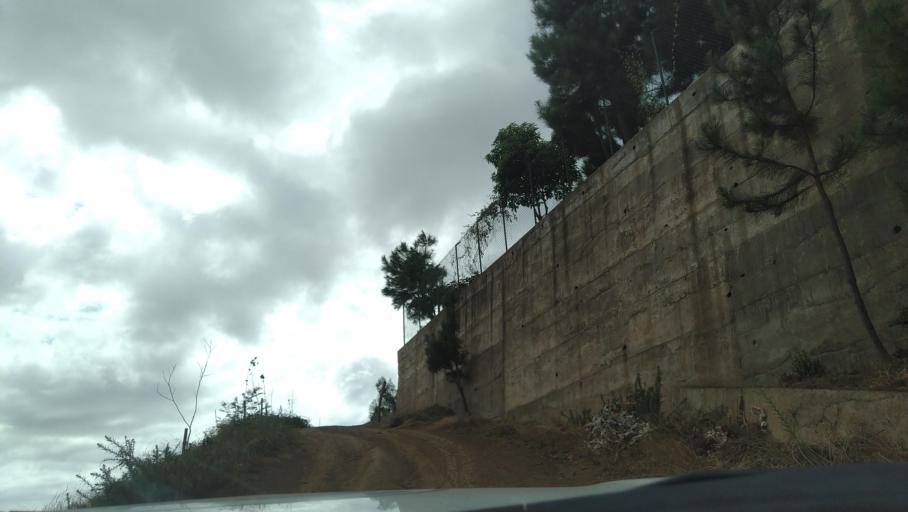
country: PT
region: Madeira
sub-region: Funchal
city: Nossa Senhora do Monte
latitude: 32.6834
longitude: -16.9279
